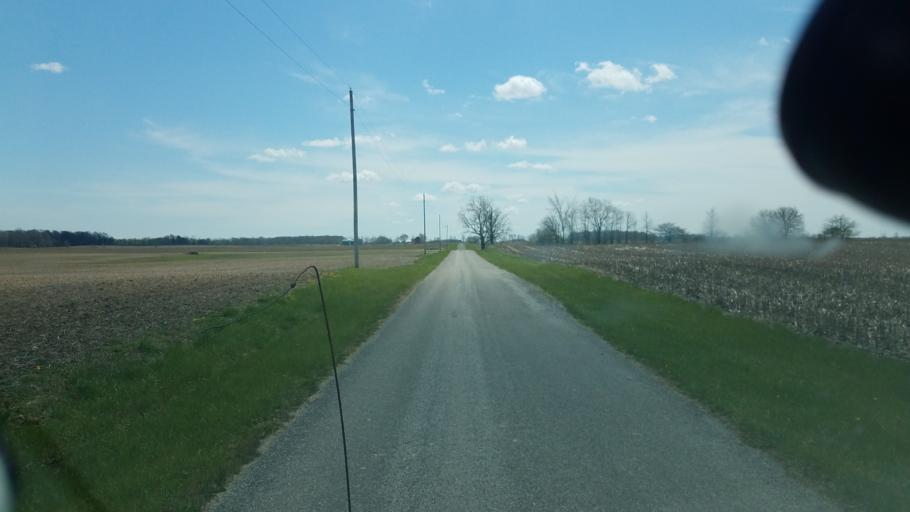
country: US
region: Ohio
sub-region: Union County
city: Richwood
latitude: 40.5249
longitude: -83.3615
